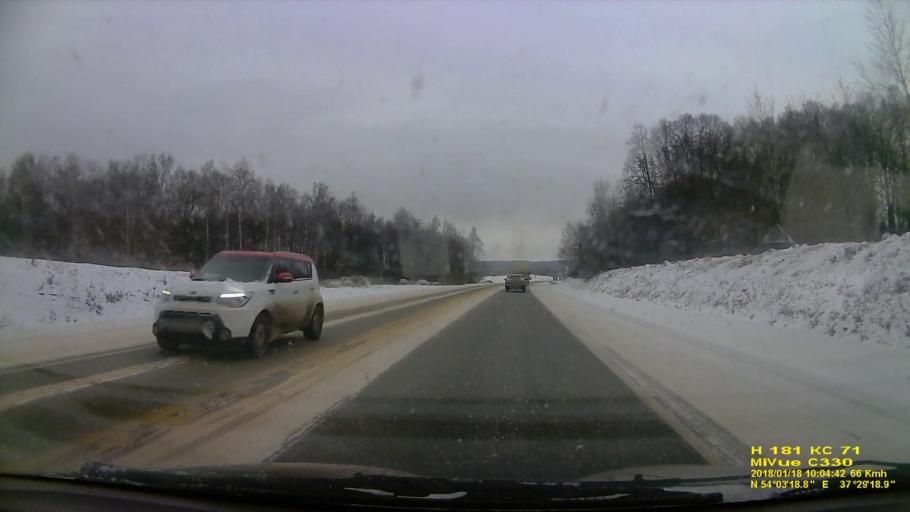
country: RU
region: Tula
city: Pervomayskiy
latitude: 54.0551
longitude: 37.4886
